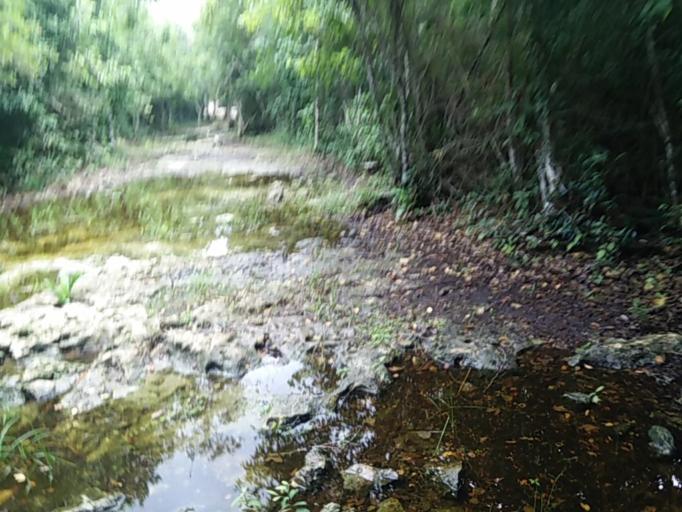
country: MX
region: Quintana Roo
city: San Miguel de Cozumel
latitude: 20.5029
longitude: -86.8442
